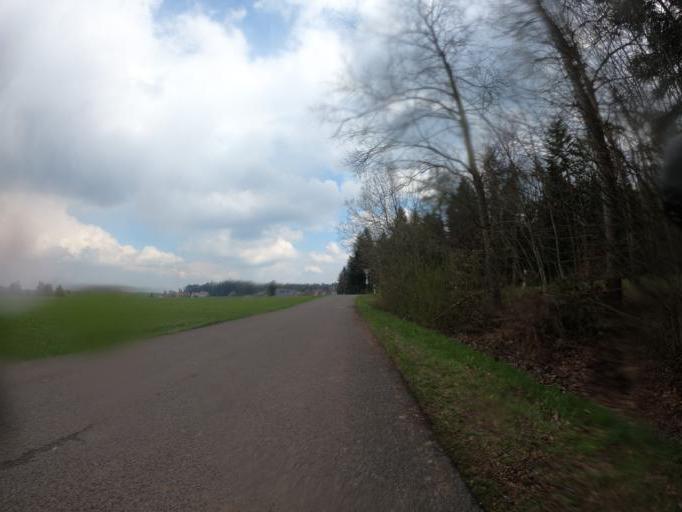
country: DE
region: Baden-Wuerttemberg
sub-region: Karlsruhe Region
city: Oberreichenbach
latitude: 48.7448
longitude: 8.6560
